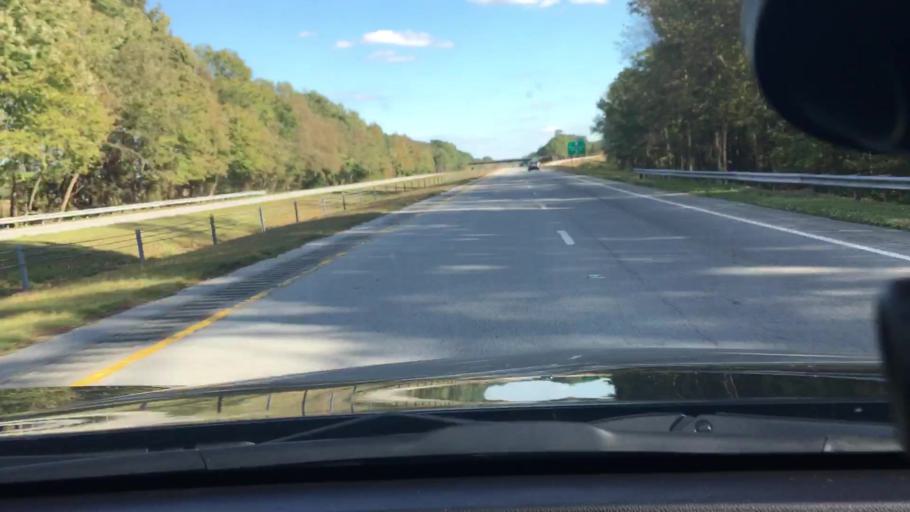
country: US
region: North Carolina
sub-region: Pitt County
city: Farmville
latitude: 35.6183
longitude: -77.6851
